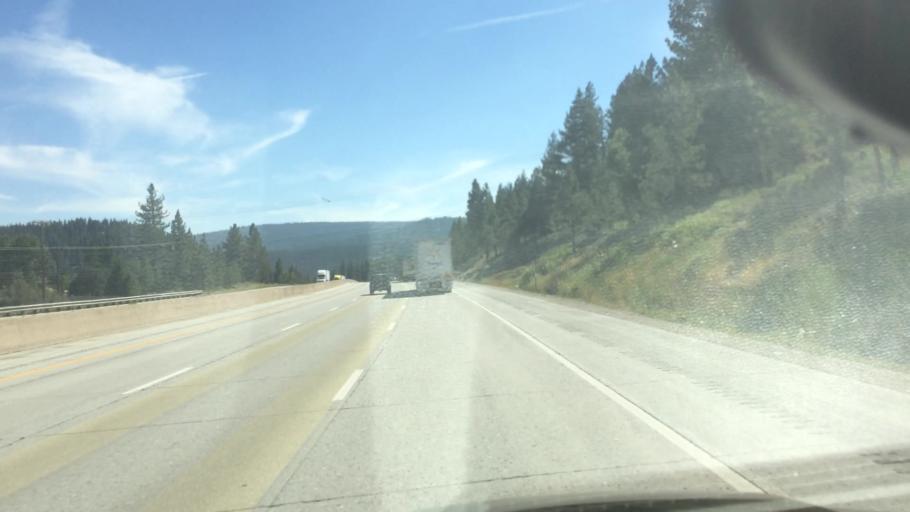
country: US
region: California
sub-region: Nevada County
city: Truckee
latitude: 39.3292
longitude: -120.1888
